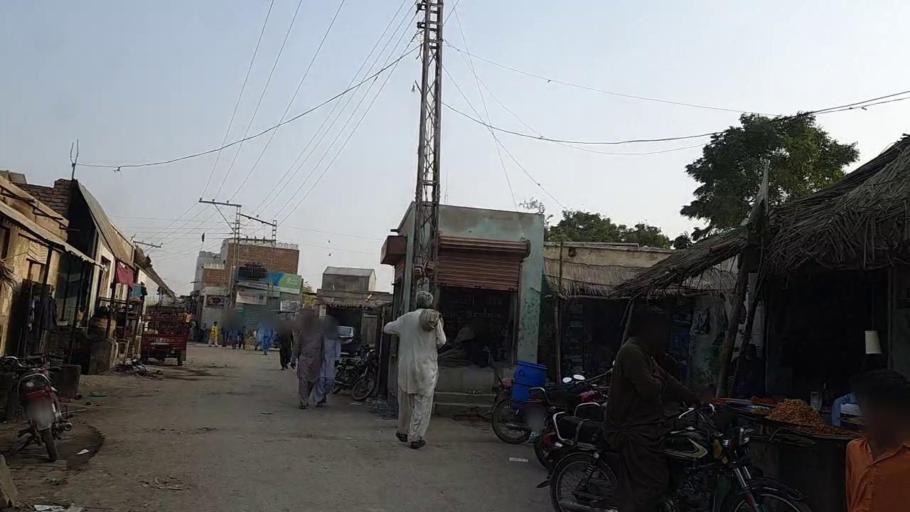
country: PK
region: Sindh
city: Naukot
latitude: 24.6576
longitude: 69.2898
